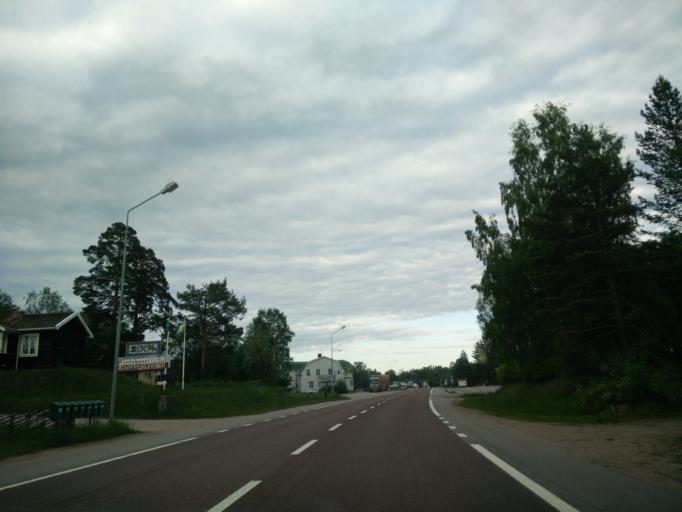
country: SE
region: Jaemtland
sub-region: Harjedalens Kommun
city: Sveg
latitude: 62.1741
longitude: 14.9392
